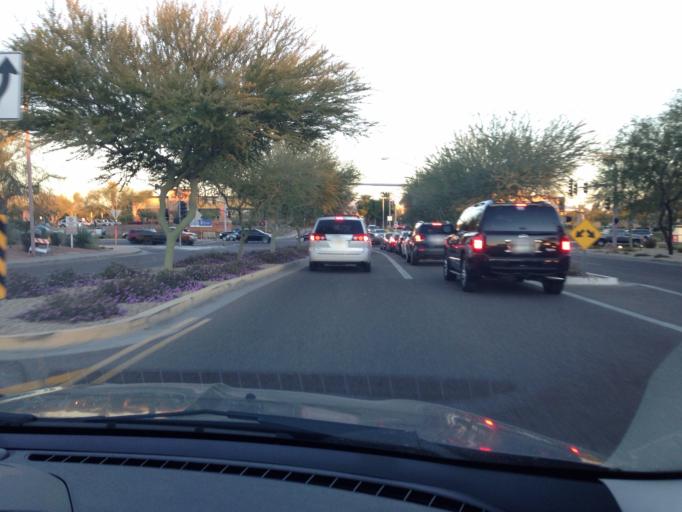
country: US
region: Arizona
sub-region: Maricopa County
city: Paradise Valley
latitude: 33.6768
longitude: -111.9784
